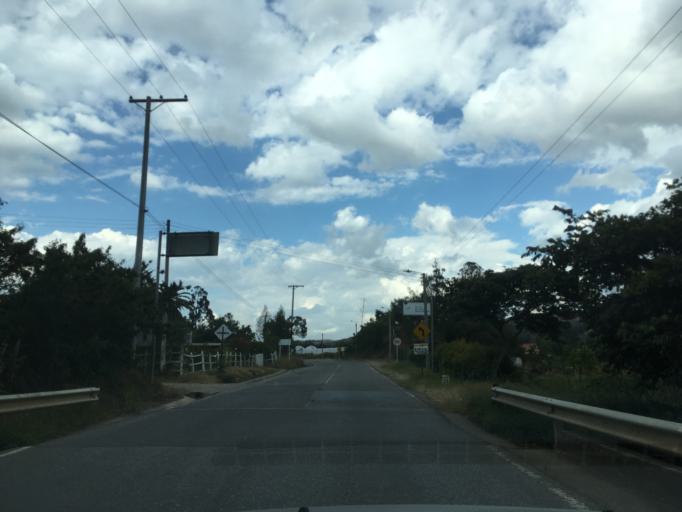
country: CO
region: Boyaca
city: Sutamarchan
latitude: 5.5834
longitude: -73.6433
